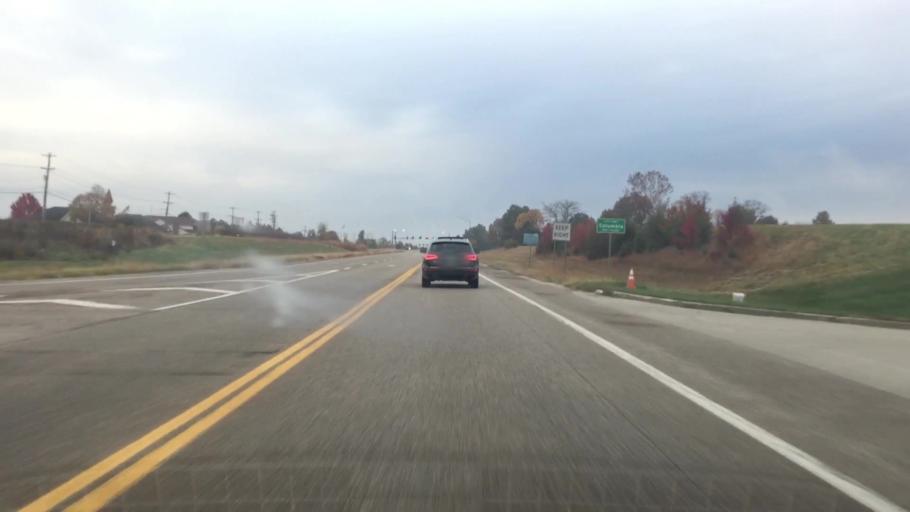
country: US
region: Missouri
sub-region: Boone County
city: Columbia
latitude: 38.8956
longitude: -92.3352
